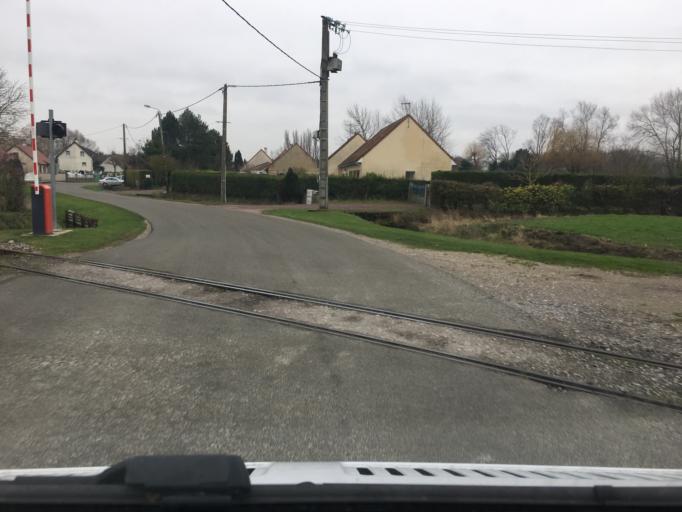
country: FR
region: Picardie
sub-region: Departement de la Somme
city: Pende
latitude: 50.1667
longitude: 1.5525
